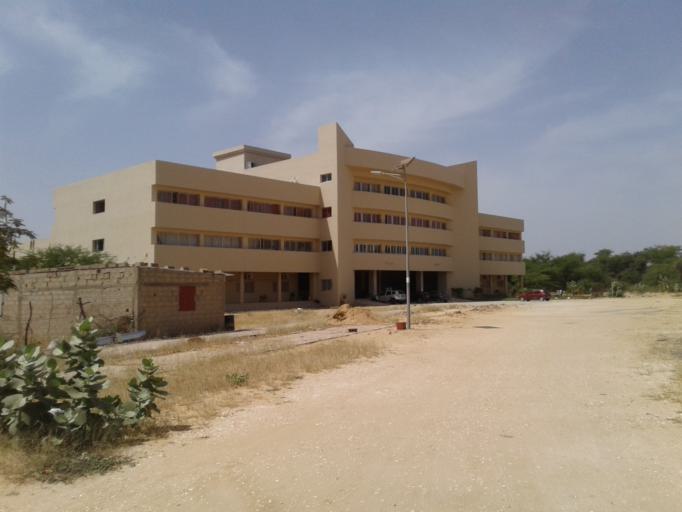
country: SN
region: Saint-Louis
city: Saint-Louis
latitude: 16.0603
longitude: -16.4245
